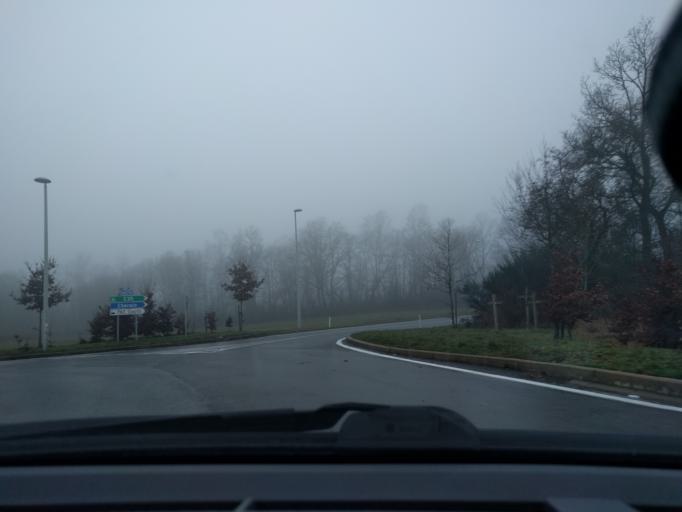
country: BE
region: Wallonia
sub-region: Province du Luxembourg
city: Gouvy
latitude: 50.2063
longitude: 5.9196
